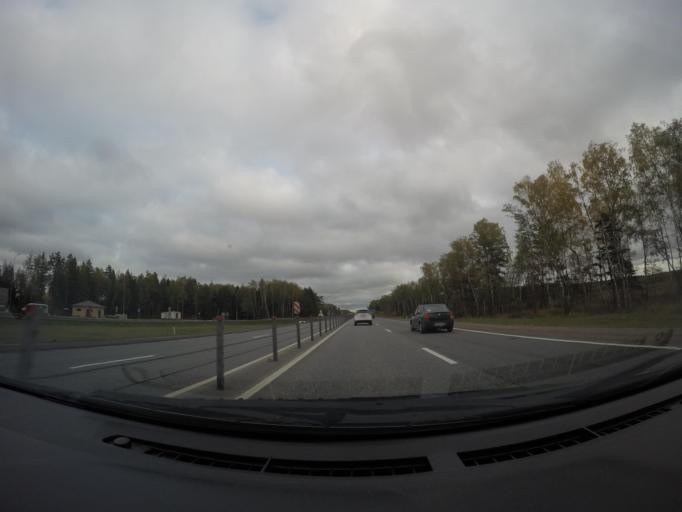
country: RU
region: Moskovskaya
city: Chupryakovo
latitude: 55.5605
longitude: 36.5982
